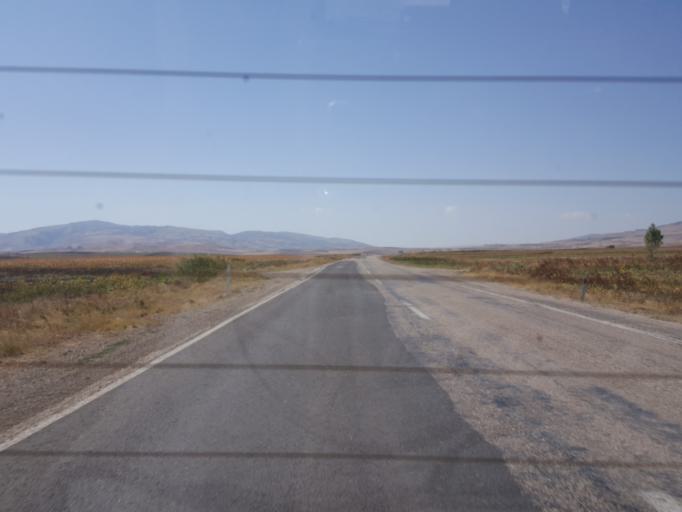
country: TR
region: Amasya
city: Dogantepe
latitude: 40.5781
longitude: 35.6272
